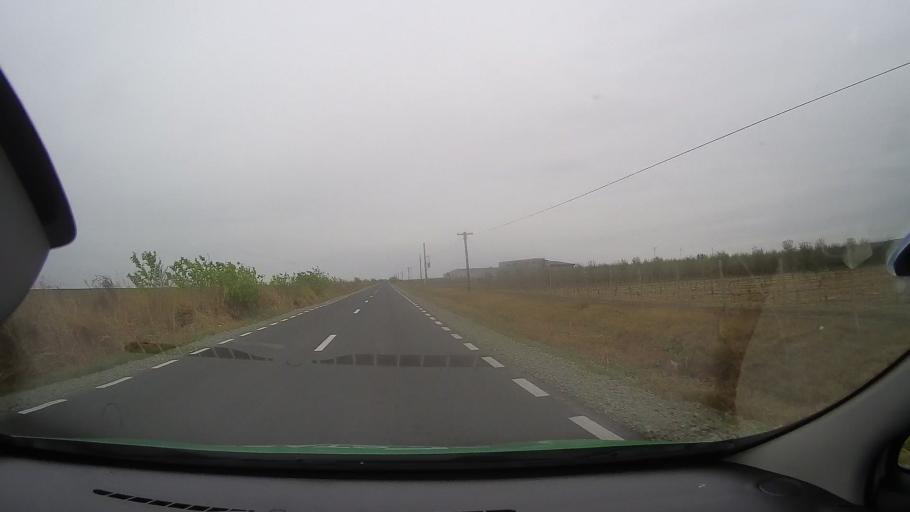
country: RO
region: Constanta
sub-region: Comuna Tortoman
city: Tortoman
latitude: 44.3660
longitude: 28.2084
